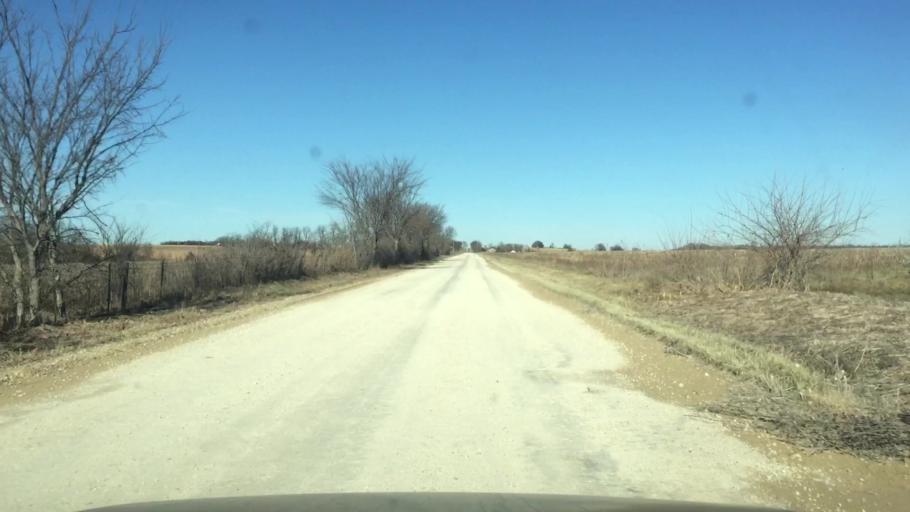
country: US
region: Kansas
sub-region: Allen County
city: Iola
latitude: 37.8682
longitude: -95.3910
